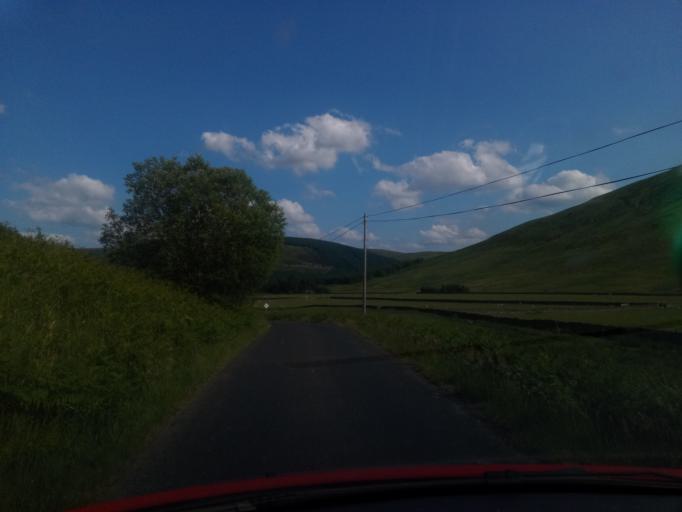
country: GB
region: Scotland
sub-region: The Scottish Borders
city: Peebles
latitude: 55.4969
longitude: -3.2144
